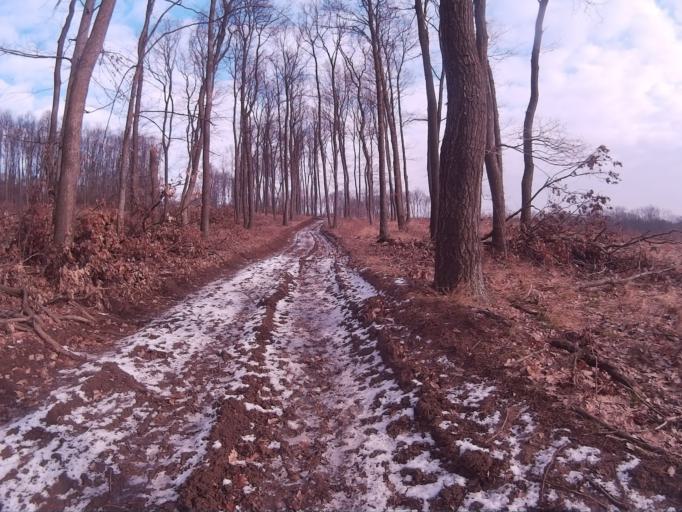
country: HU
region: Komarom-Esztergom
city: Tarjan
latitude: 47.6707
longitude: 18.5043
